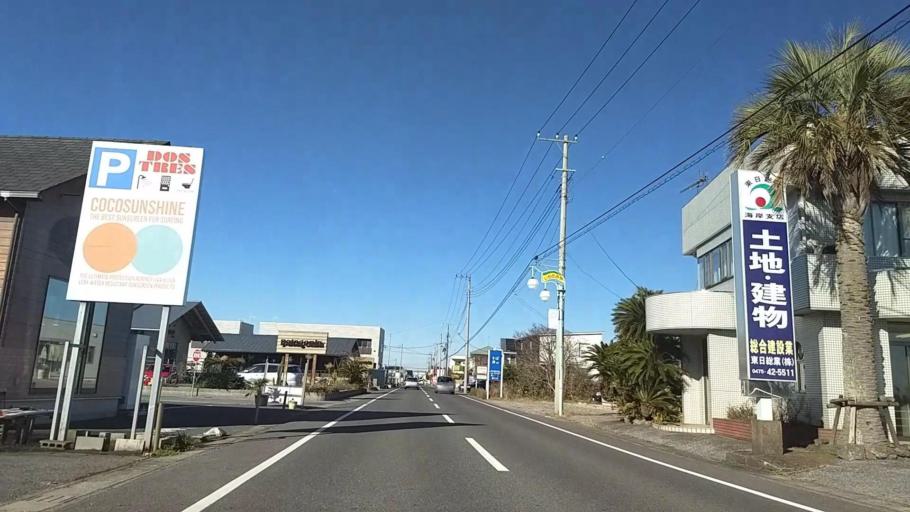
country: JP
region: Chiba
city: Ohara
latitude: 35.3525
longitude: 140.3894
